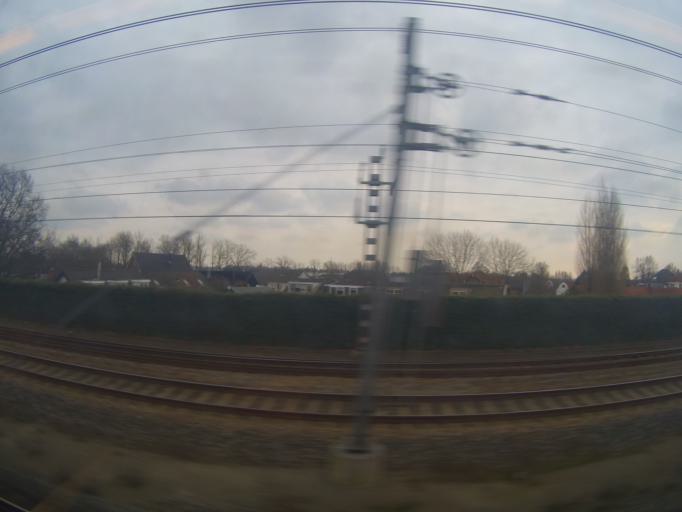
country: NL
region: Utrecht
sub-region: Gemeente Montfoort
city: Montfoort
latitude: 52.1014
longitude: 4.9423
